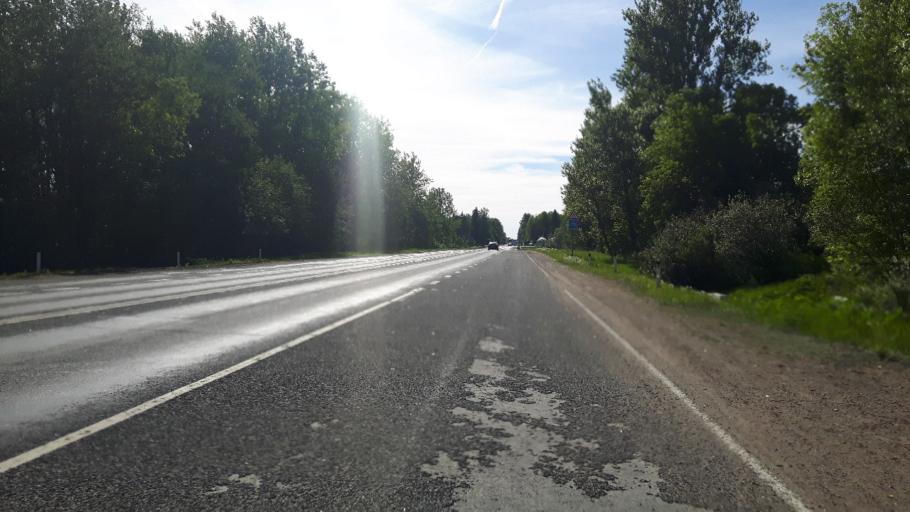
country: RU
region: Leningrad
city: Ivangorod
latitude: 59.3807
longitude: 28.3225
